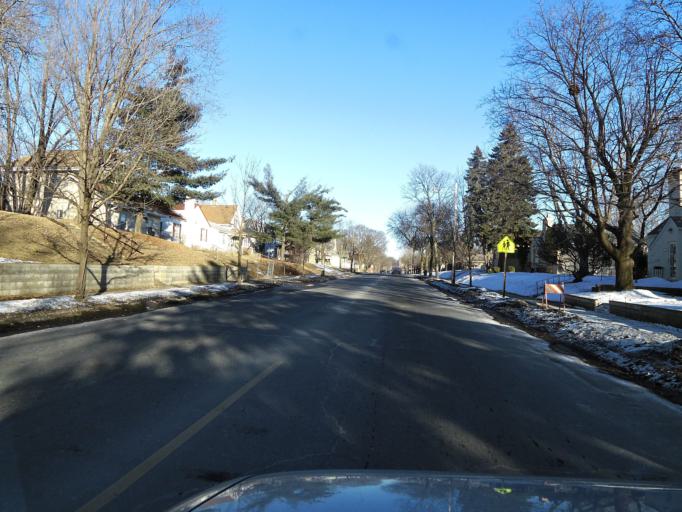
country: US
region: Minnesota
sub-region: Ramsey County
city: Maplewood
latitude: 44.9631
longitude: -93.0452
